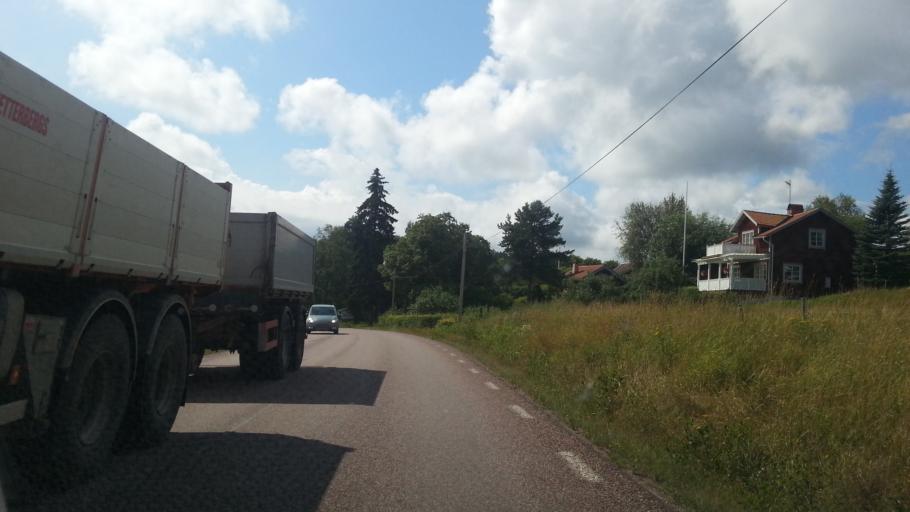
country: SE
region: Dalarna
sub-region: Faluns Kommun
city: Falun
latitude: 60.6341
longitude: 15.7696
